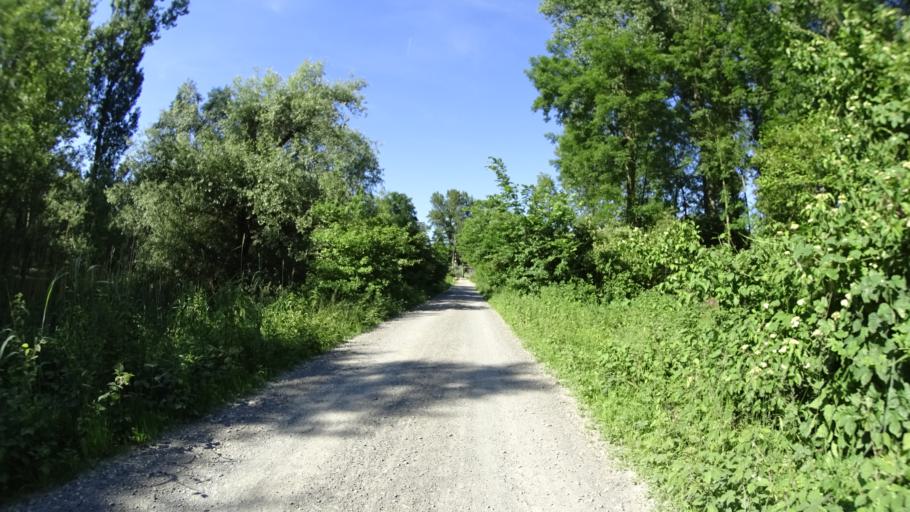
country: DE
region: Baden-Wuerttemberg
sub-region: Karlsruhe Region
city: Eggenstein-Leopoldshafen
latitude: 49.1016
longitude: 8.3690
